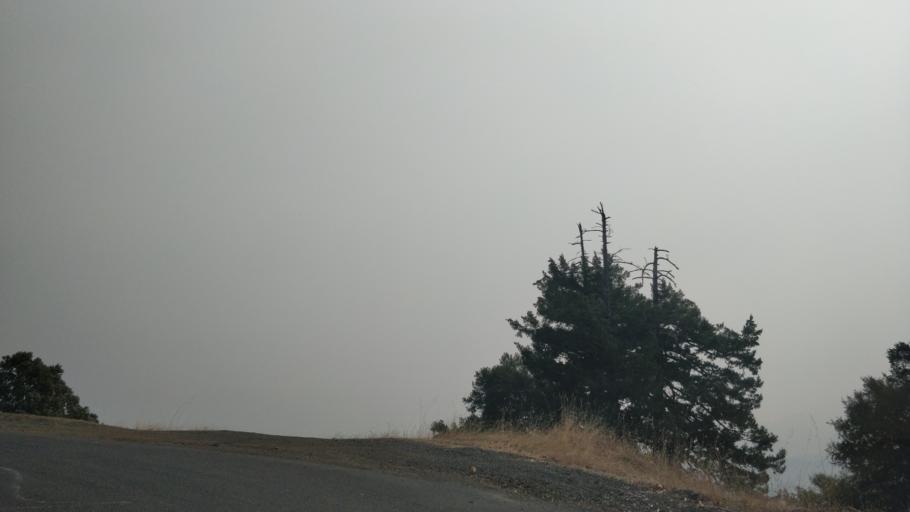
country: US
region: California
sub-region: Humboldt County
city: Rio Dell
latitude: 40.2528
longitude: -124.1180
